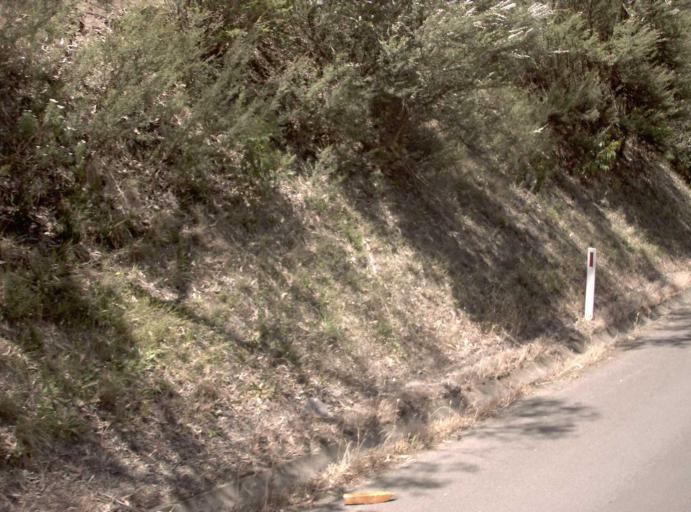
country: AU
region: Victoria
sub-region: Latrobe
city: Moe
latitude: -38.1953
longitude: 146.2862
